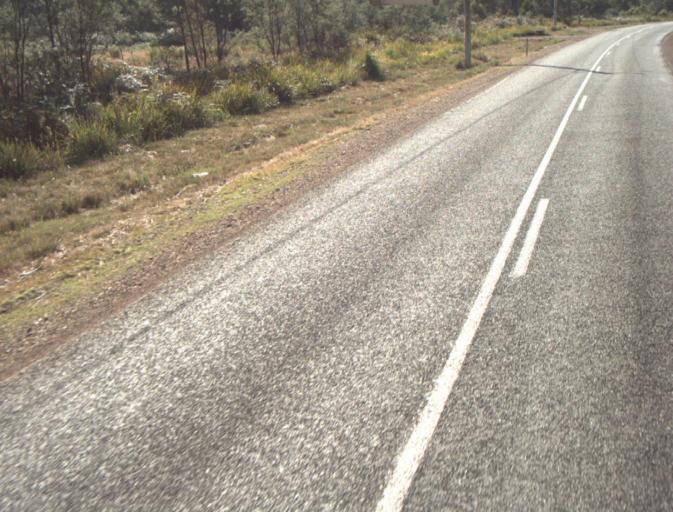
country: AU
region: Tasmania
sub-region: Launceston
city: Mayfield
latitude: -41.3100
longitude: 147.1337
